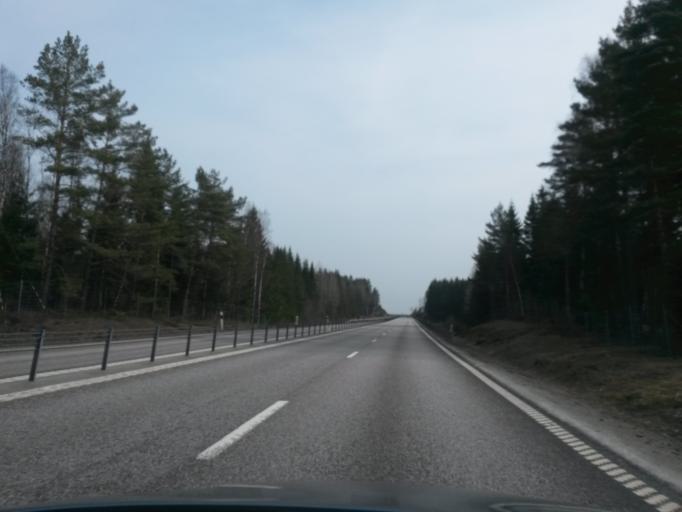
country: SE
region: Vaestra Goetaland
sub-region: Gullspangs Kommun
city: Anderstorp
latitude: 58.8940
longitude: 14.3206
